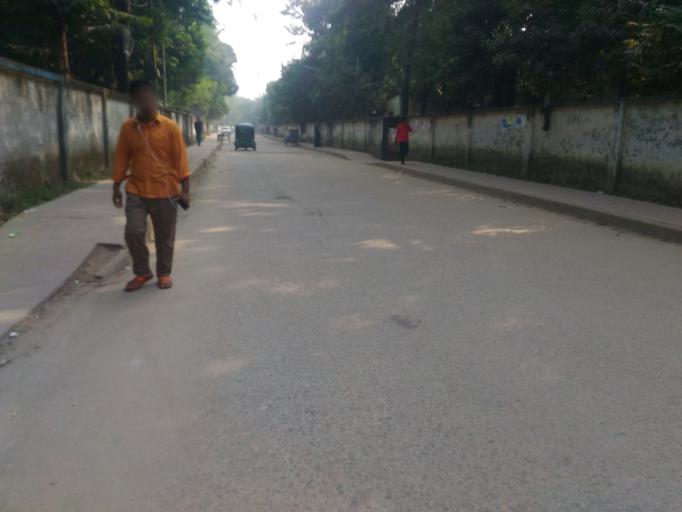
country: BD
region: Dhaka
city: Paltan
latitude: 23.7884
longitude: 90.4064
